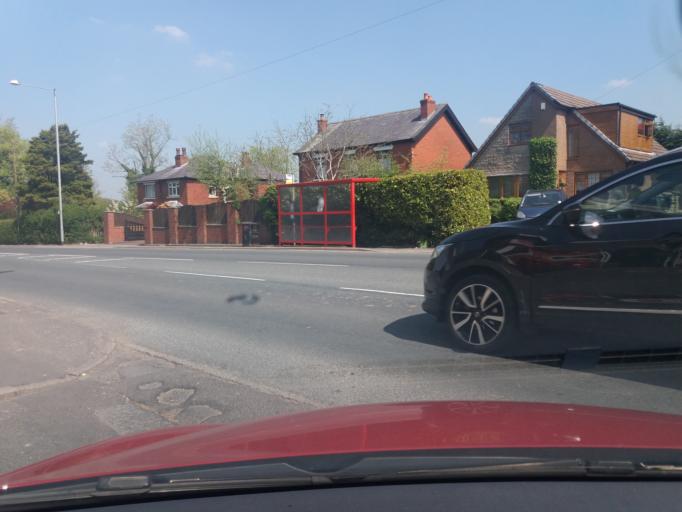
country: GB
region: England
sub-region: Lancashire
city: Chorley
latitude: 53.6766
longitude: -2.6353
